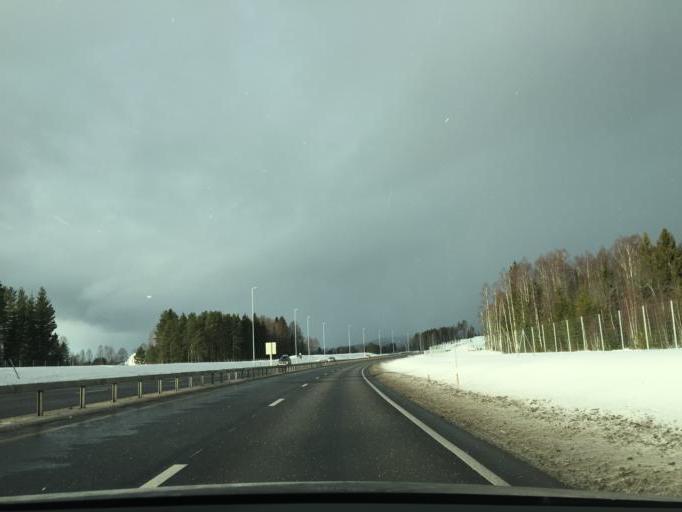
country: NO
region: Hedmark
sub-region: Kongsvinger
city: Spetalen
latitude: 60.2151
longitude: 11.8727
